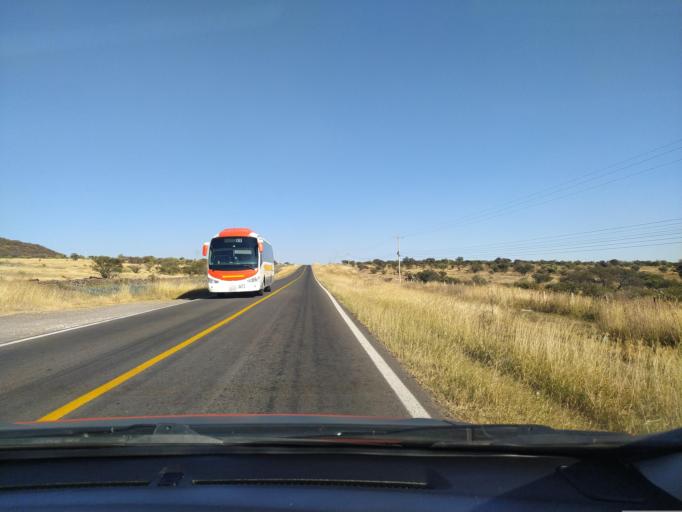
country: MX
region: Jalisco
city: San Miguel el Alto
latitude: 21.0230
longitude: -102.4397
